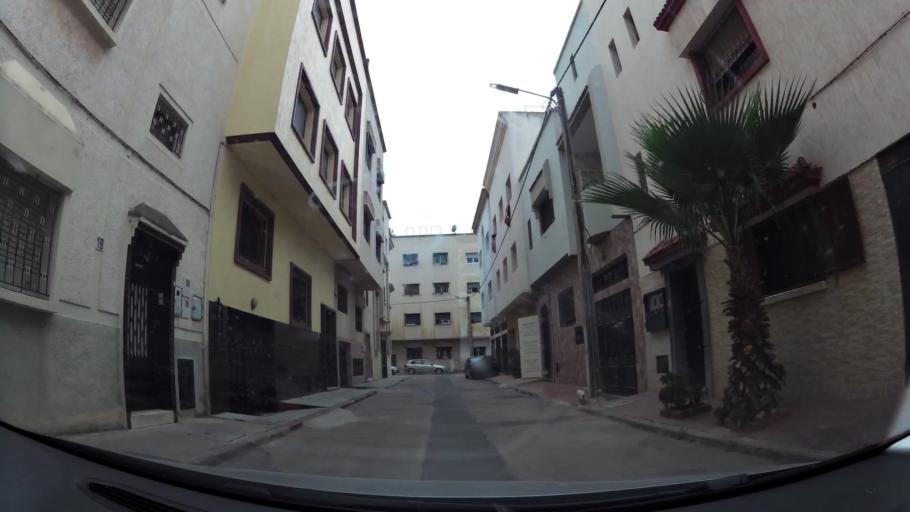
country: MA
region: Rabat-Sale-Zemmour-Zaer
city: Sale
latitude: 34.0302
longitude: -6.8004
